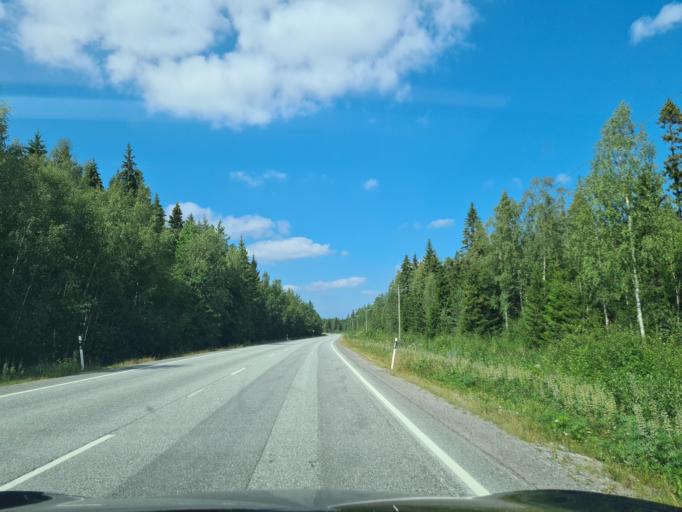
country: FI
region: Ostrobothnia
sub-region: Vaasa
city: Vaasa
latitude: 63.1743
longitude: 21.5786
